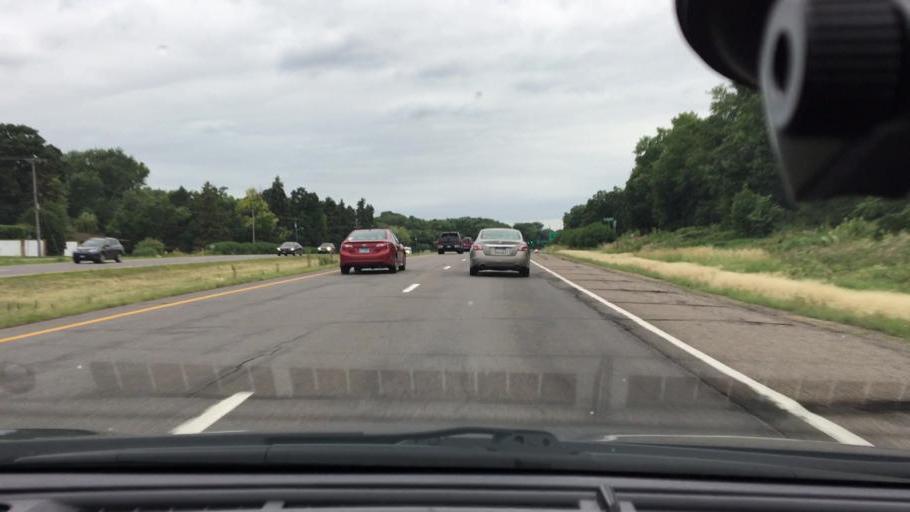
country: US
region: Minnesota
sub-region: Hennepin County
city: Golden Valley
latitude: 44.9839
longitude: -93.3663
